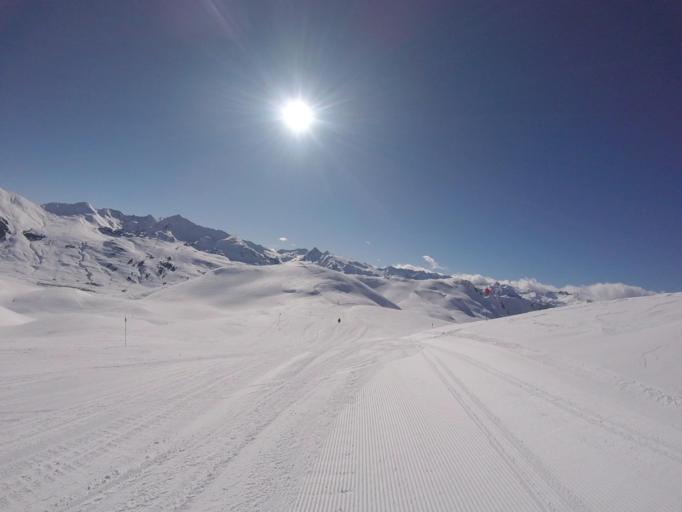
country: ES
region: Catalonia
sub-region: Provincia de Lleida
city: Vielha
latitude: 42.7302
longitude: 0.9390
